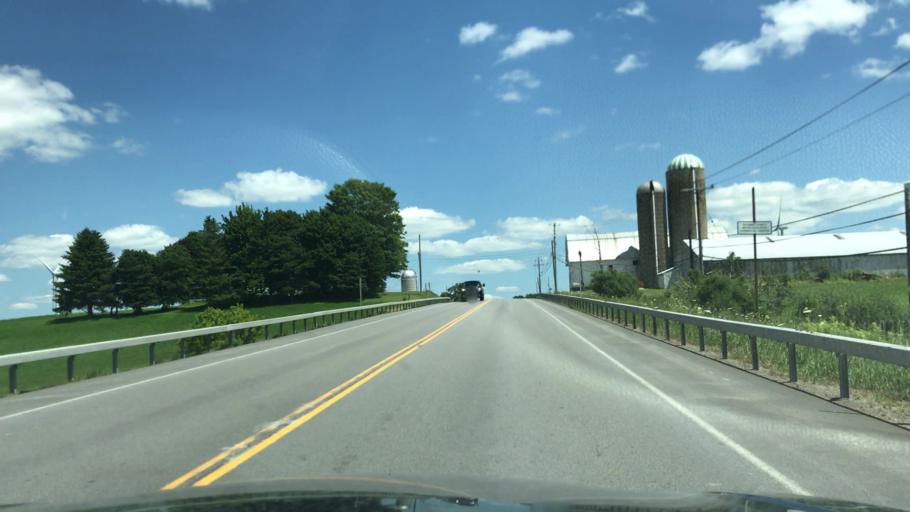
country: US
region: New York
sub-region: Erie County
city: Alden
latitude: 42.7700
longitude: -78.4180
